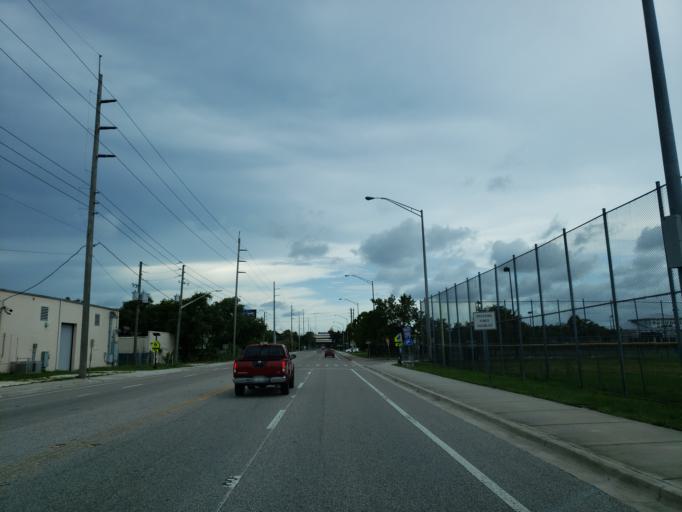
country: US
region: Florida
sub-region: Pinellas County
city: Saint Petersburg
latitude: 27.7622
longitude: -82.6754
